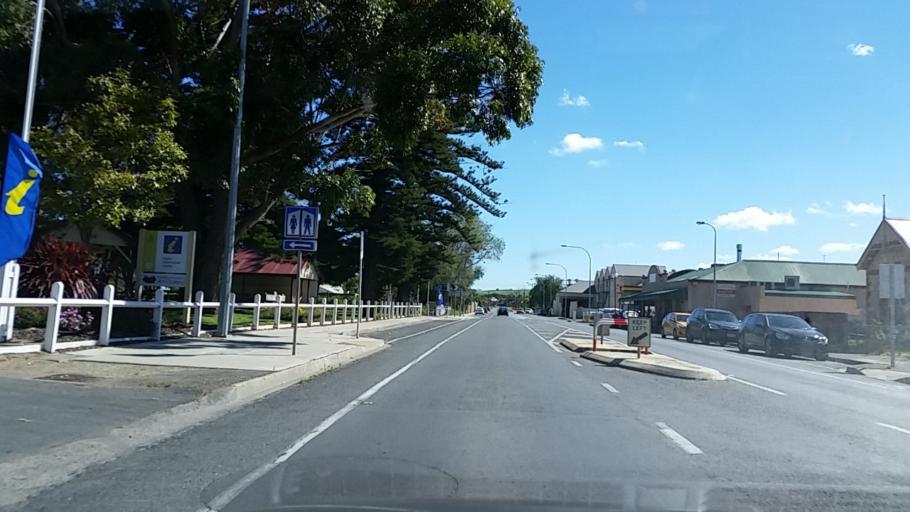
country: AU
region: South Australia
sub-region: Alexandrina
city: Strathalbyn
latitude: -35.2606
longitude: 138.8924
